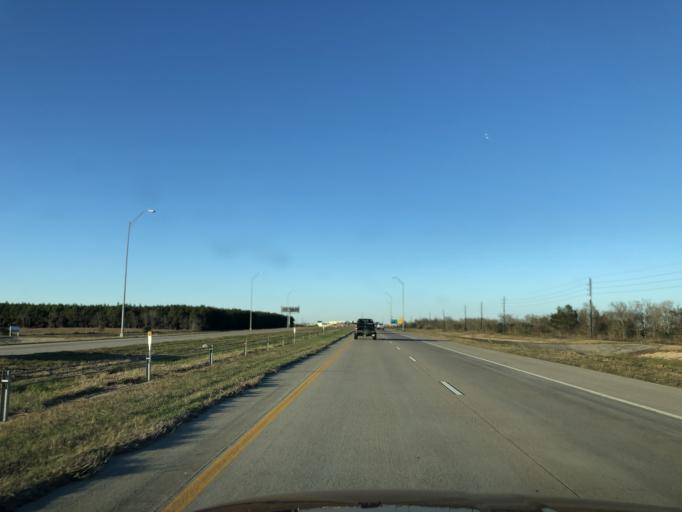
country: US
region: Texas
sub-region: Harris County
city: Cypress
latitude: 29.8966
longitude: -95.7580
